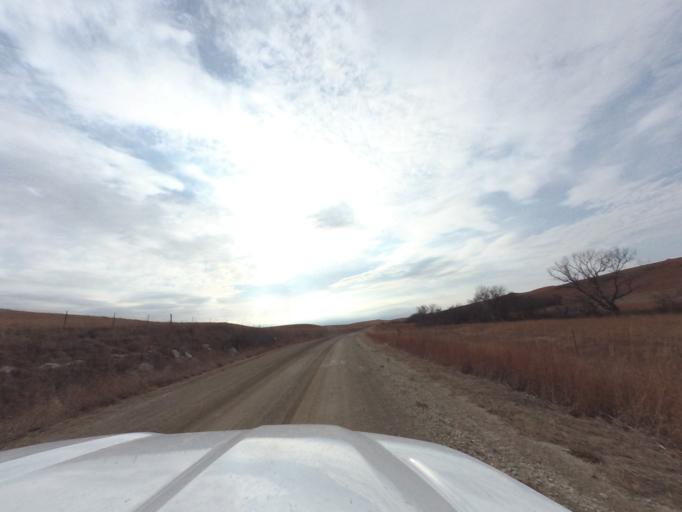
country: US
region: Kansas
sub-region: Chase County
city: Cottonwood Falls
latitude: 38.2622
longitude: -96.7271
